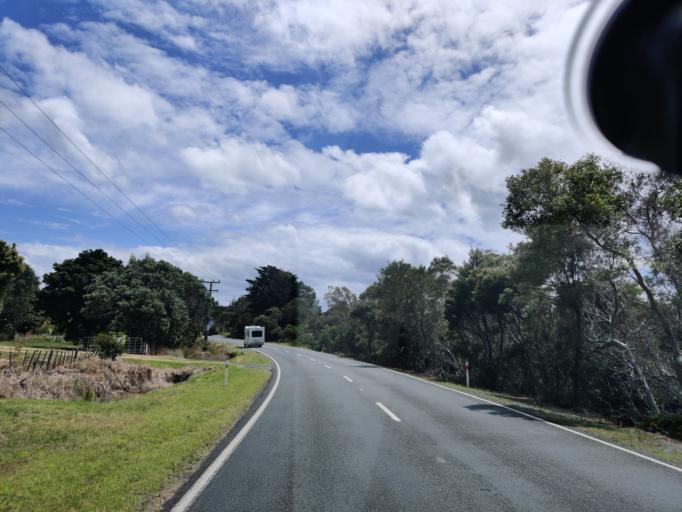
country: NZ
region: Northland
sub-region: Far North District
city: Kaitaia
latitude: -34.7861
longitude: 173.0995
